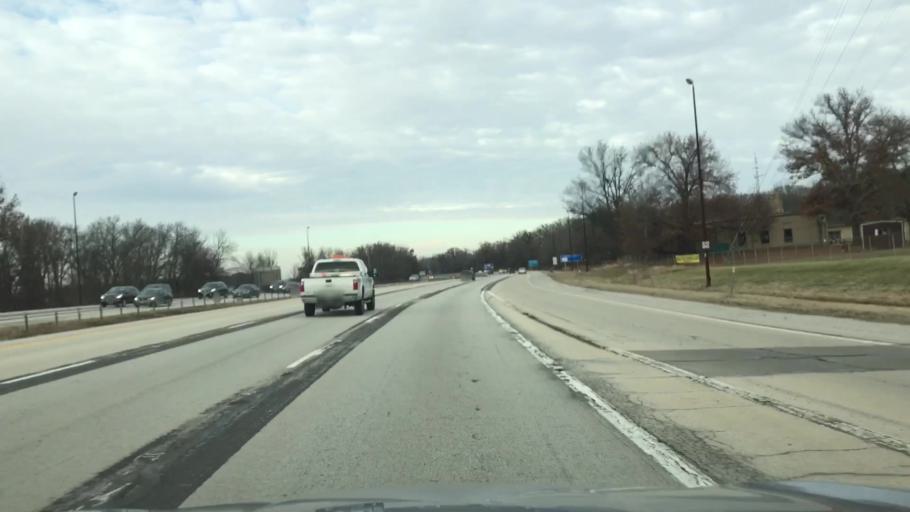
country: US
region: Illinois
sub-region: Sangamon County
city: Chatham
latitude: 39.6893
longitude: -89.6432
